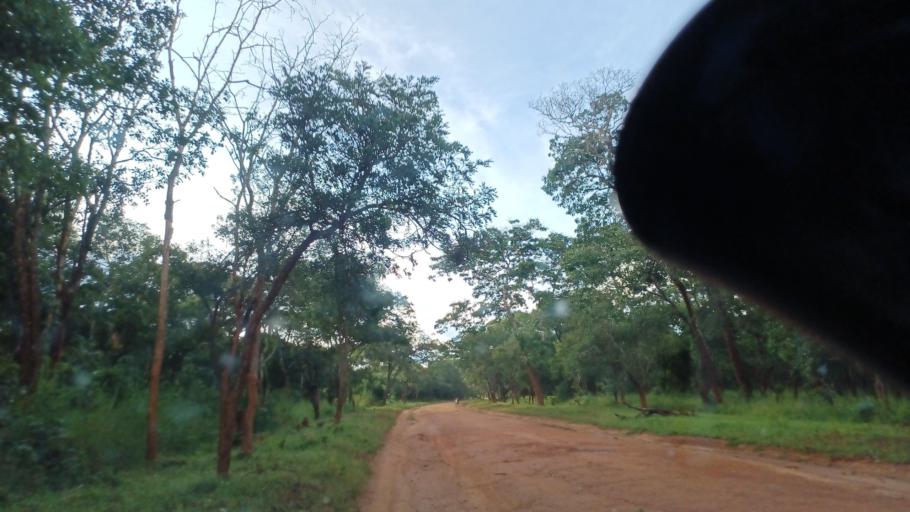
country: ZM
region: North-Western
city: Kasempa
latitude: -13.5820
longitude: 26.1176
